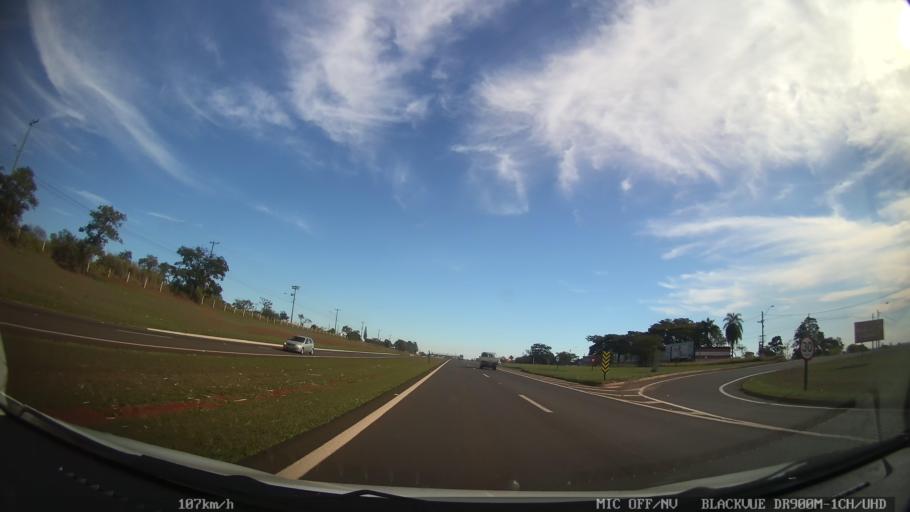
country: BR
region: Sao Paulo
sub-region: Araraquara
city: Araraquara
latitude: -21.7978
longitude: -48.1398
